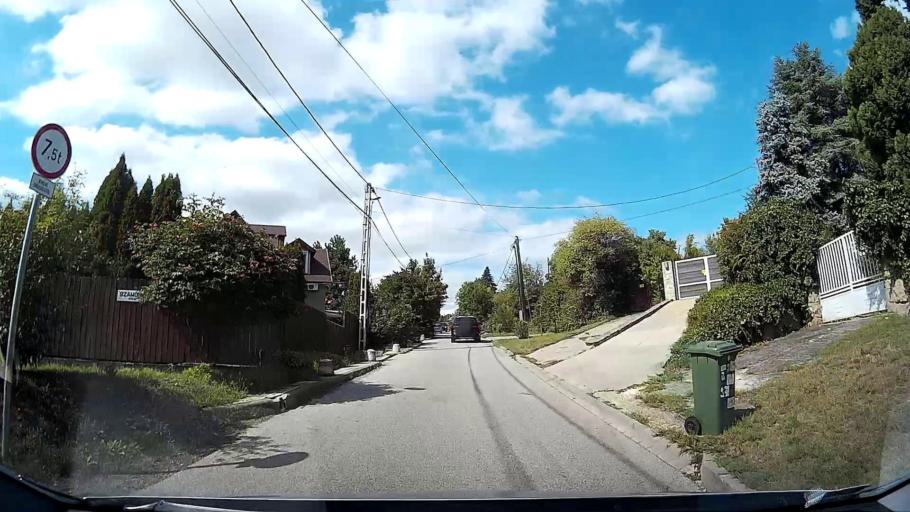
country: HU
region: Pest
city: Szentendre
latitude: 47.6866
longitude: 19.0739
